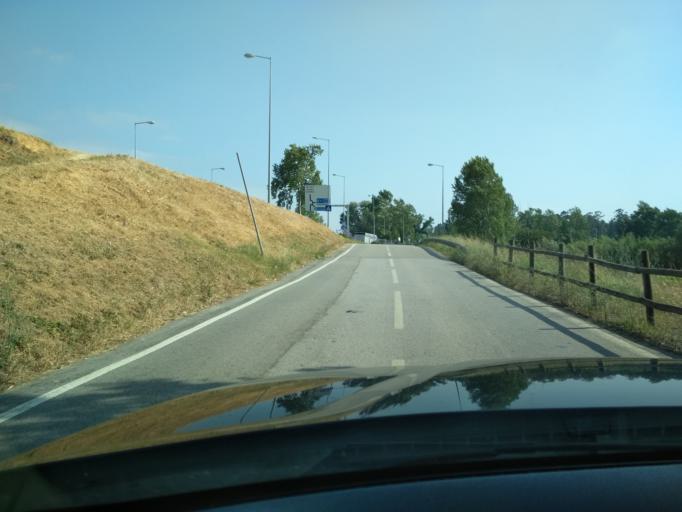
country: PT
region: Aveiro
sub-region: Mealhada
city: Mealhada
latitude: 40.3685
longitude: -8.4547
